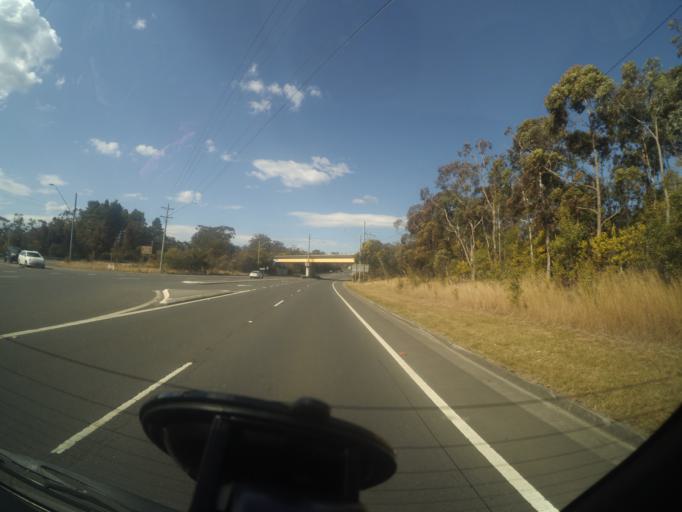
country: AU
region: New South Wales
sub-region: Blue Mountains Municipality
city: Leura
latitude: -33.7096
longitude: 150.3508
